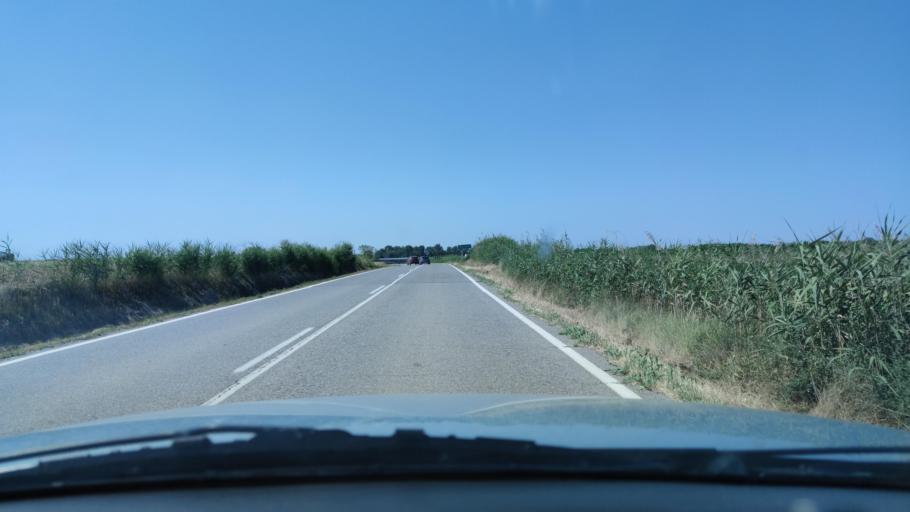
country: ES
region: Catalonia
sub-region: Provincia de Lleida
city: Ivars d'Urgell
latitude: 41.7050
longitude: 0.9820
